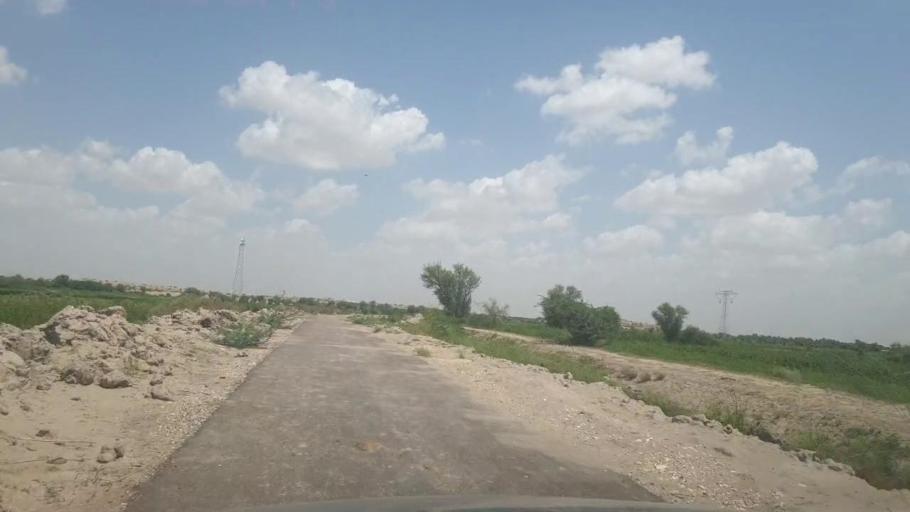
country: PK
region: Sindh
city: Kot Diji
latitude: 27.2335
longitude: 69.0397
